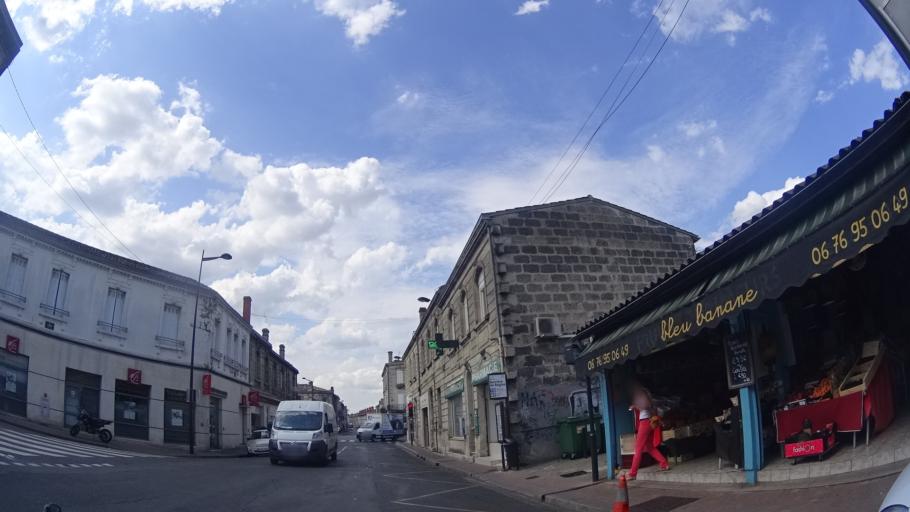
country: FR
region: Aquitaine
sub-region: Departement de la Gironde
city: Begles
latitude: 44.8128
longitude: -0.5645
